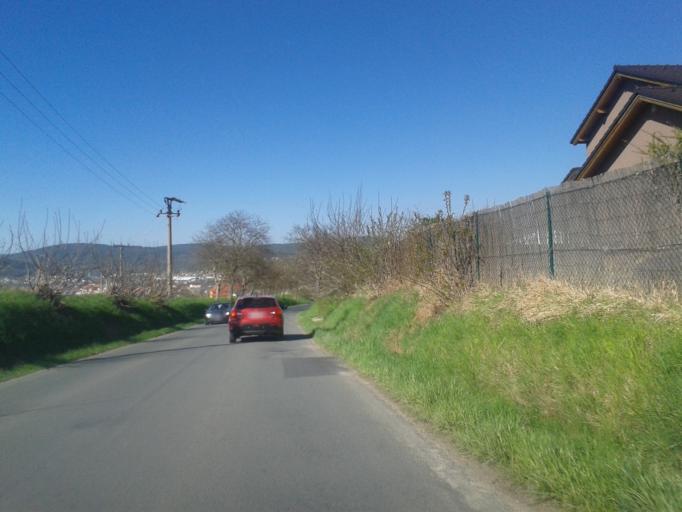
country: CZ
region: Central Bohemia
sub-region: Okres Beroun
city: Beroun
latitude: 49.9446
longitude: 14.0692
